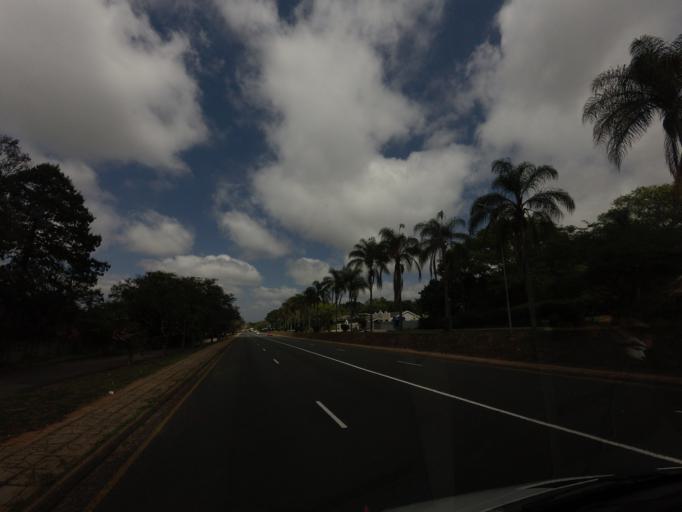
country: ZA
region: Mpumalanga
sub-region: Ehlanzeni District
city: White River
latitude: -25.3338
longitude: 31.0061
